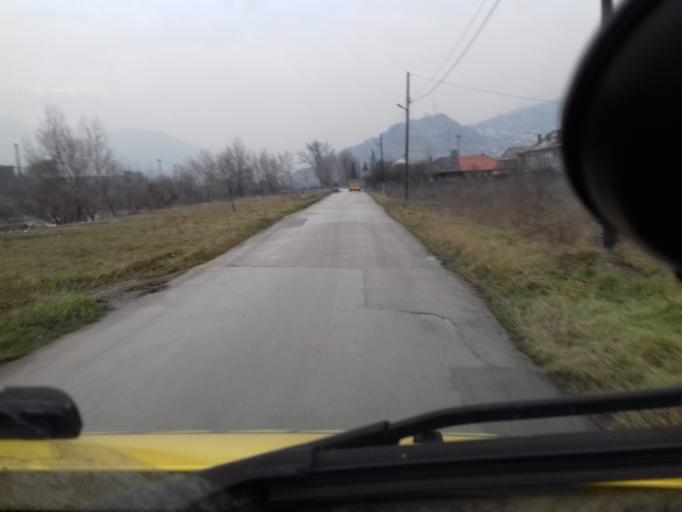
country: BA
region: Federation of Bosnia and Herzegovina
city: Zenica
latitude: 44.2223
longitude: 17.9085
